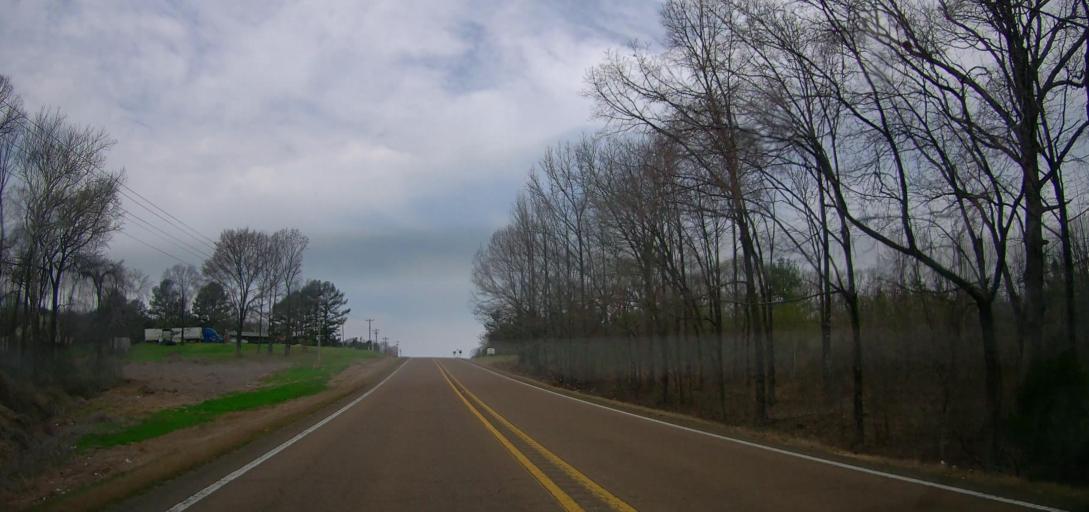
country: US
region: Mississippi
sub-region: Marshall County
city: Byhalia
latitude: 34.8595
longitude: -89.6518
